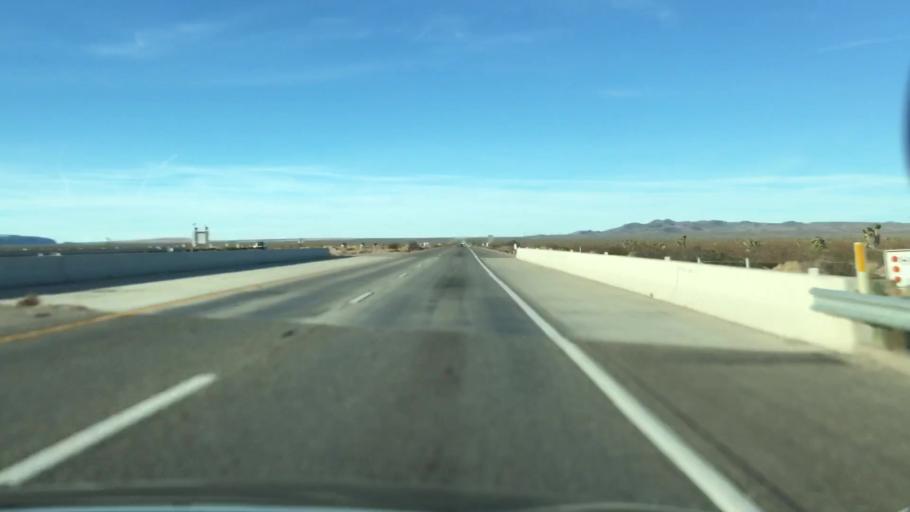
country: US
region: Nevada
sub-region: Clark County
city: Sandy Valley
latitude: 35.4324
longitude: -115.7079
